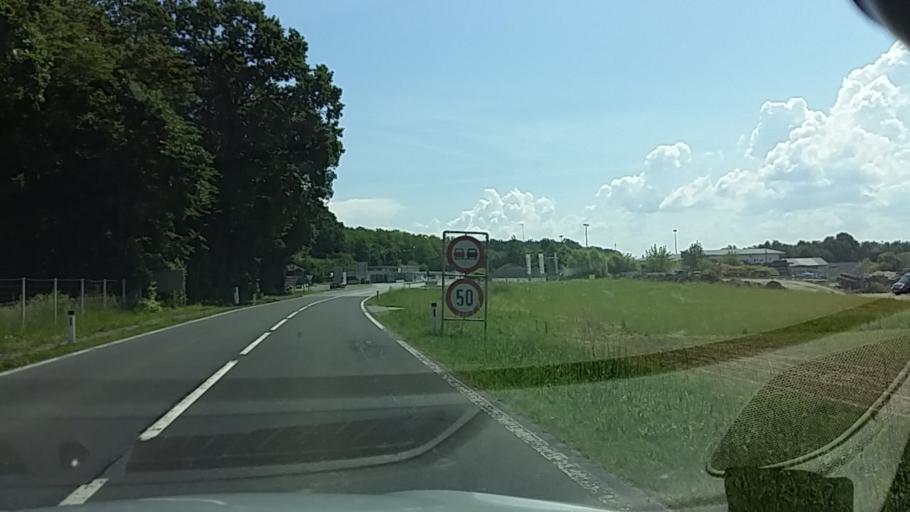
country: AT
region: Burgenland
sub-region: Politischer Bezirk Jennersdorf
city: Heiligenkreuz im Lafnitztal
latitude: 46.9857
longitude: 16.2711
